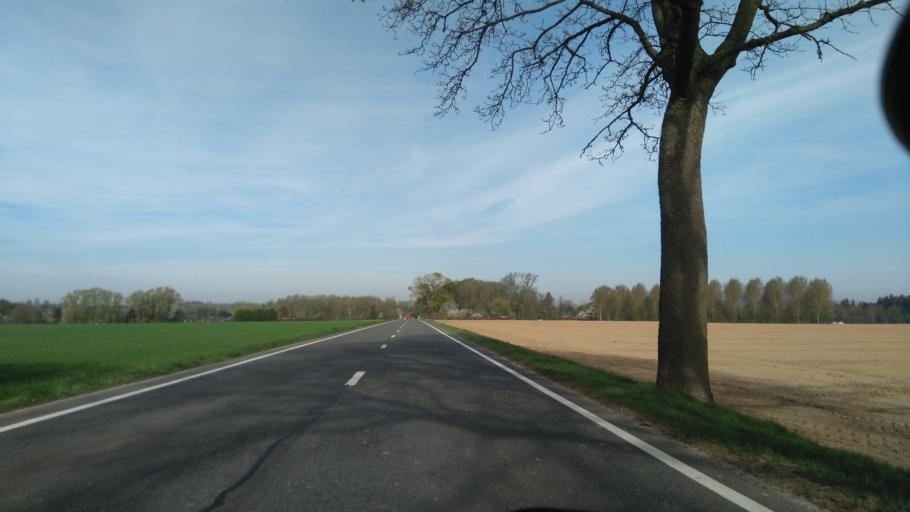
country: BE
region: Wallonia
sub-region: Province de Namur
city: Forville
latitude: 50.5774
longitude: 4.9832
